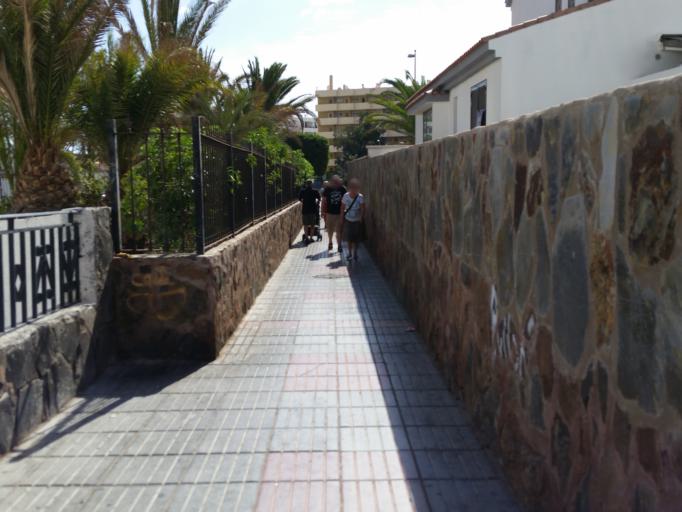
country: ES
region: Canary Islands
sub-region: Provincia de Las Palmas
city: Maspalomas
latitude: 27.7646
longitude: -15.5794
